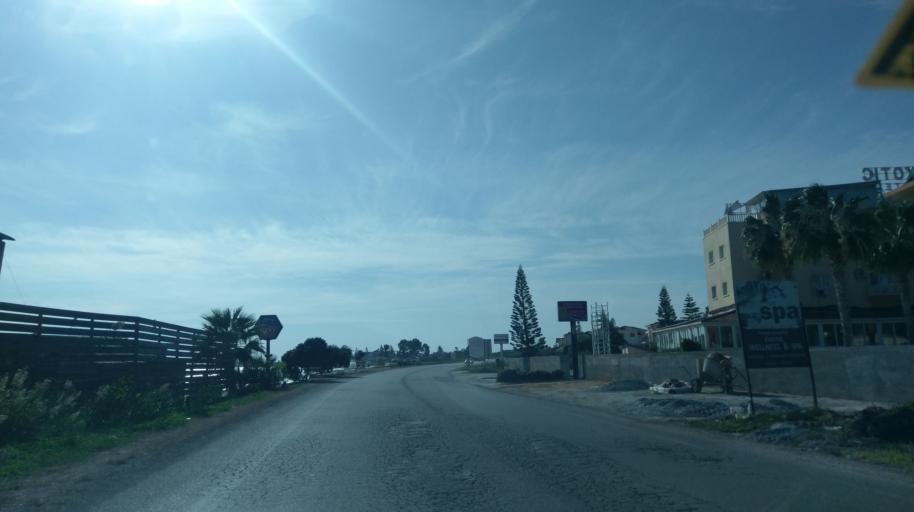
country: CY
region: Ammochostos
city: Trikomo
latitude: 35.3072
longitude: 33.9453
